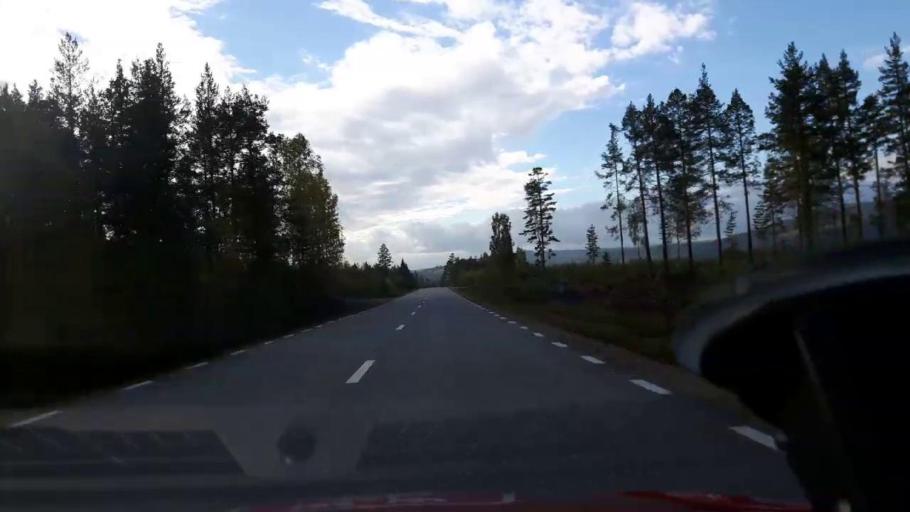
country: SE
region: Gaevleborg
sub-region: Ljusdals Kommun
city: Farila
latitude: 62.0079
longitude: 15.2404
